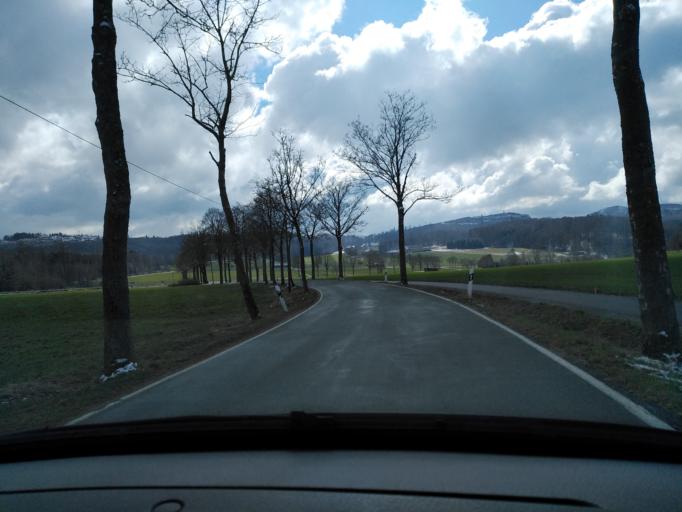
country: DE
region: North Rhine-Westphalia
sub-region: Regierungsbezirk Arnsberg
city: Brilon
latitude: 51.4016
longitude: 8.6330
